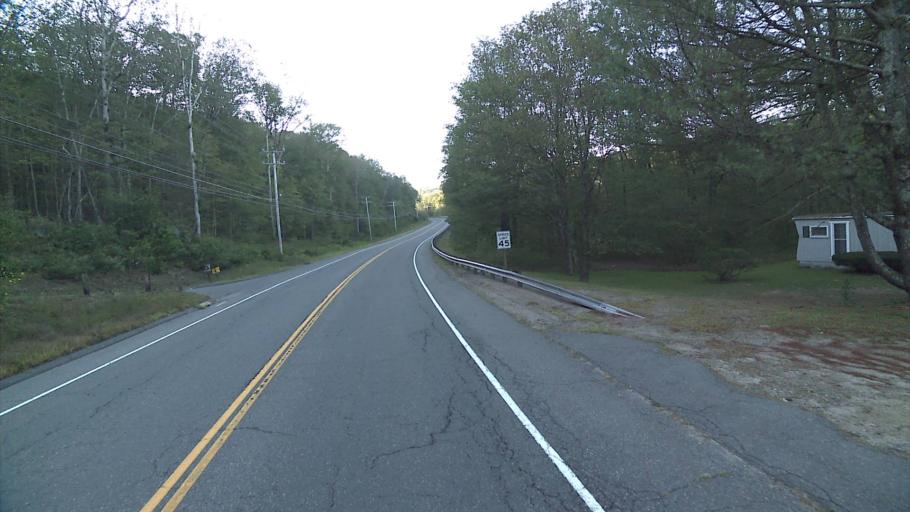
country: US
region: Connecticut
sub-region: Tolland County
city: Stafford Springs
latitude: 41.9272
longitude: -72.3055
